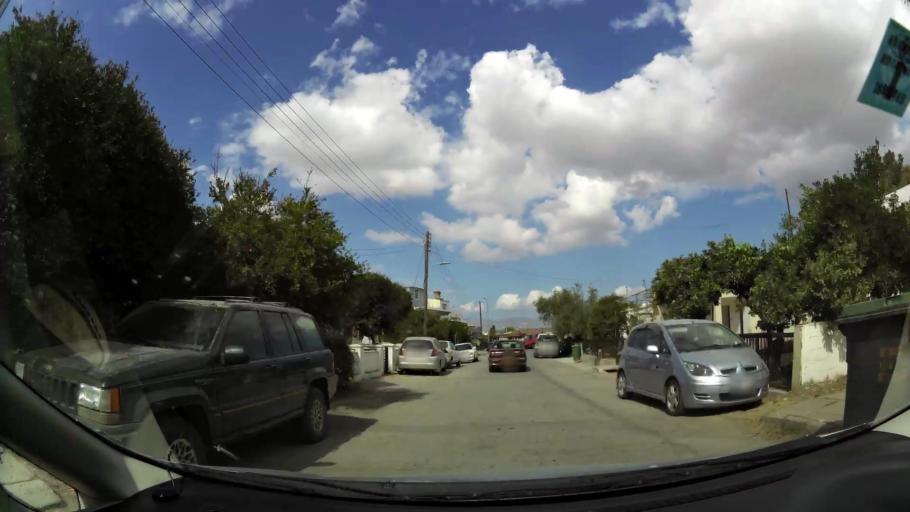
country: CY
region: Lefkosia
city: Nicosia
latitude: 35.1971
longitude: 33.3552
